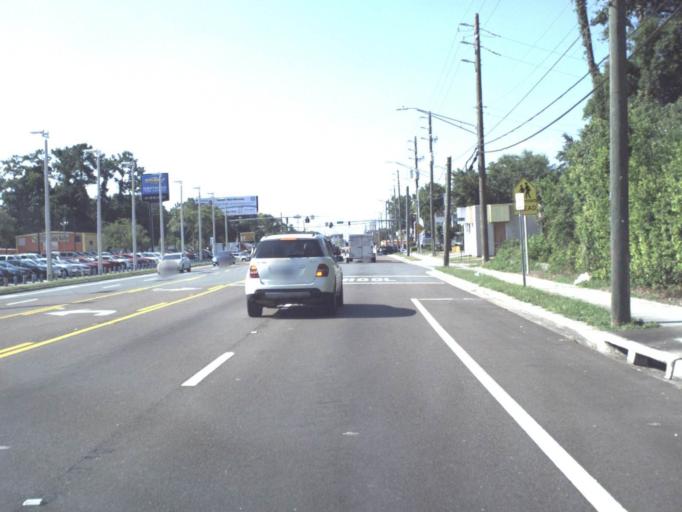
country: US
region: Florida
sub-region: Duval County
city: Jacksonville
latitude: 30.2904
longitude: -81.7303
